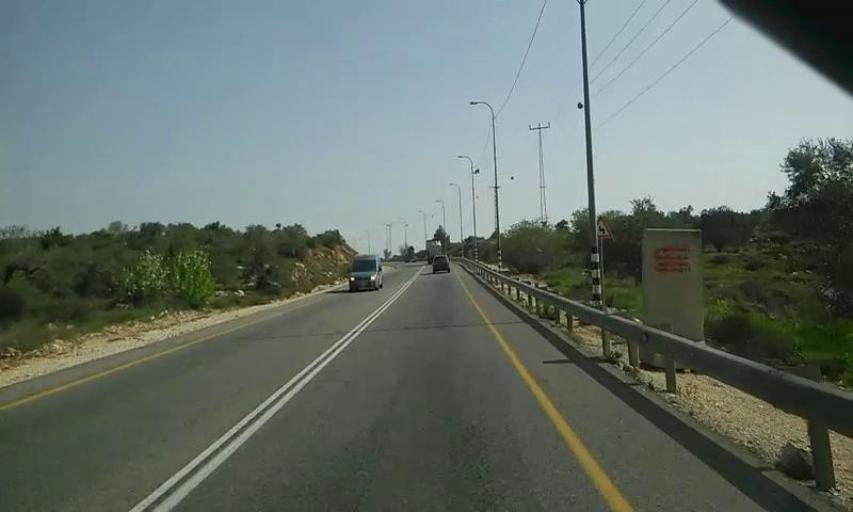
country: PS
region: West Bank
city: Turmus`ayya
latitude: 32.0427
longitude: 35.2821
